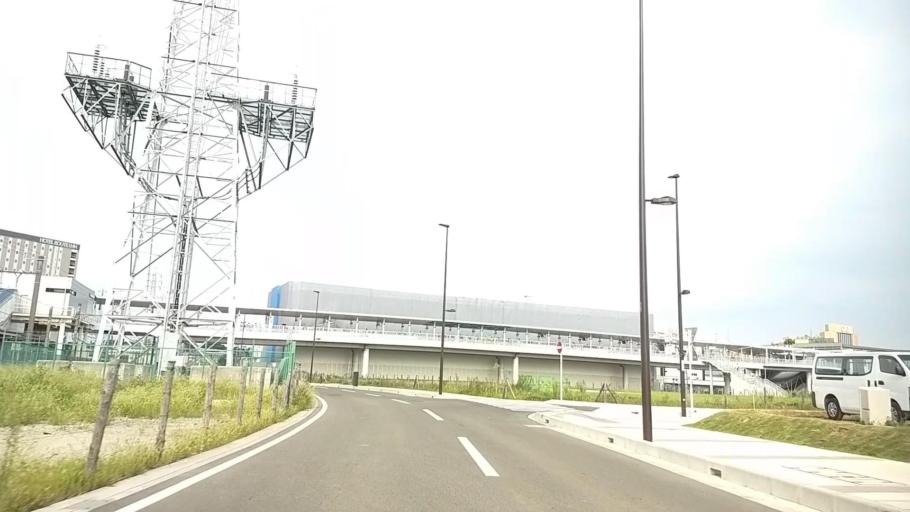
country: JP
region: Kanagawa
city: Atsugi
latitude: 35.4536
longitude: 139.3884
